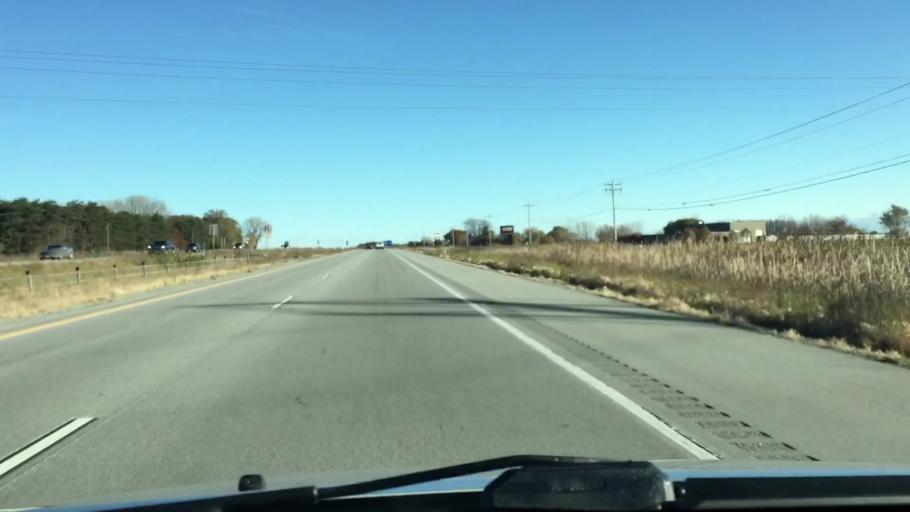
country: US
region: Wisconsin
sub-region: Brown County
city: Wrightstown
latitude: 44.3757
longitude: -88.1695
